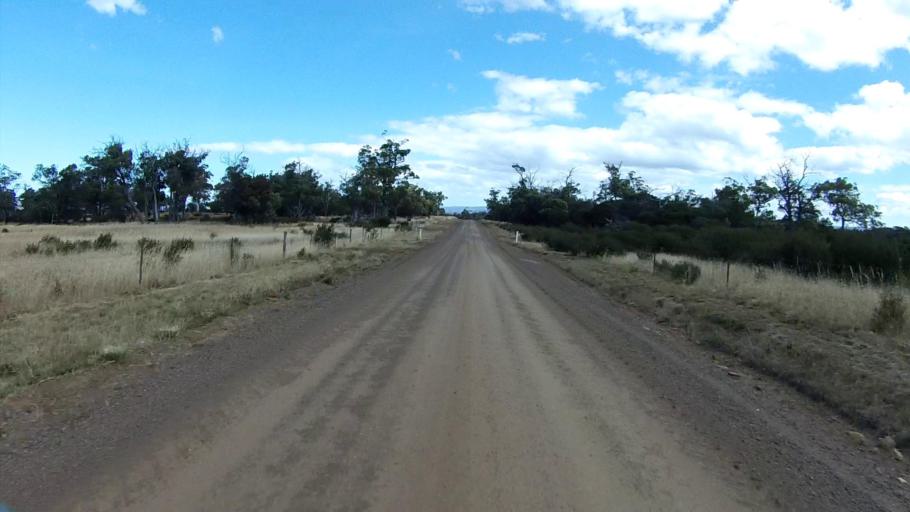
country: AU
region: Tasmania
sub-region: Break O'Day
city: St Helens
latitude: -41.9790
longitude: 148.0682
